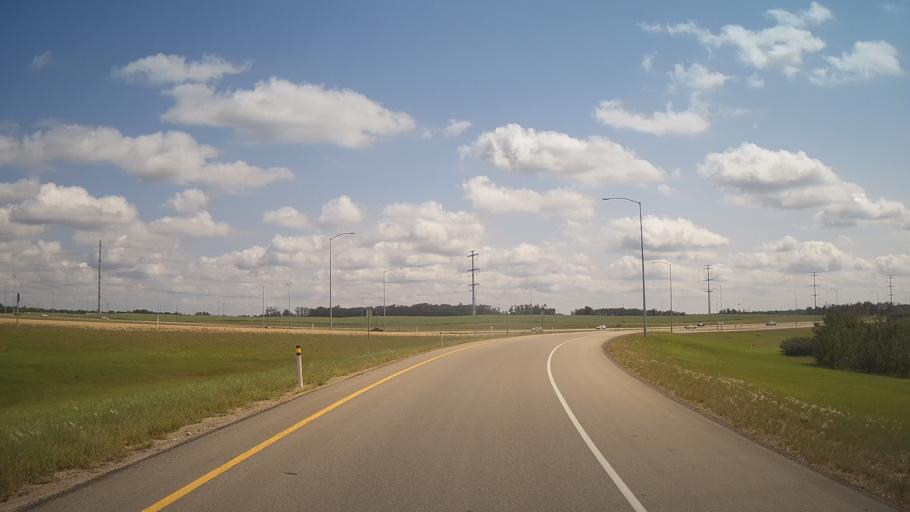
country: CA
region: Alberta
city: Sherwood Park
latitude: 53.4818
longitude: -113.3476
